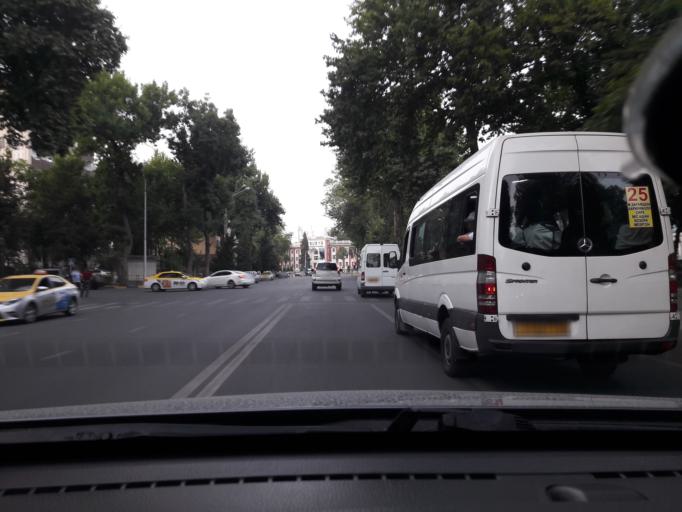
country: TJ
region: Dushanbe
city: Dushanbe
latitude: 38.5728
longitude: 68.7917
